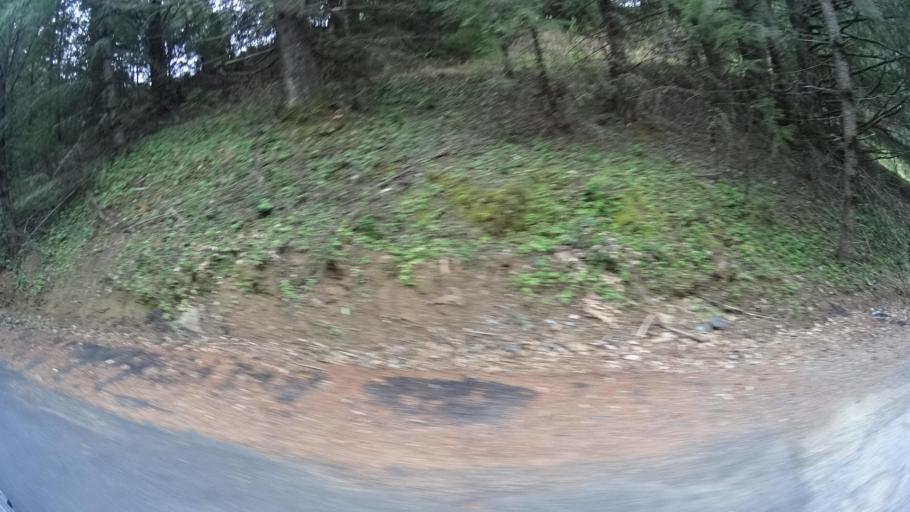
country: US
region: California
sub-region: Humboldt County
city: Redway
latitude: 40.1593
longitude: -123.5591
